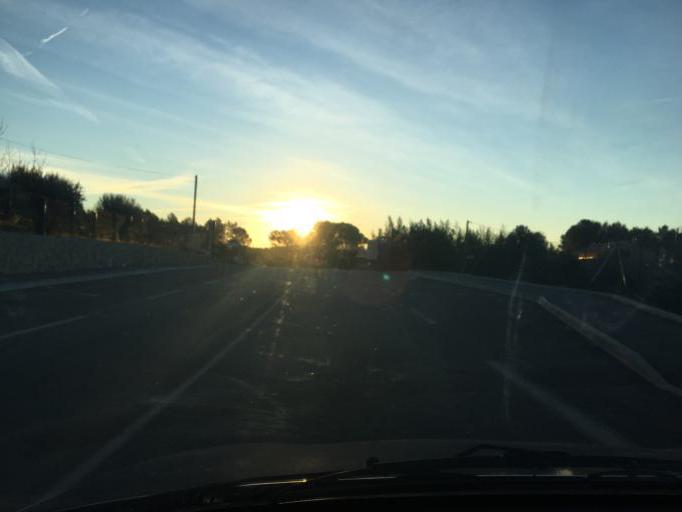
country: FR
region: Provence-Alpes-Cote d'Azur
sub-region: Departement du Var
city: Taradeau
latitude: 43.4627
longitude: 6.4019
